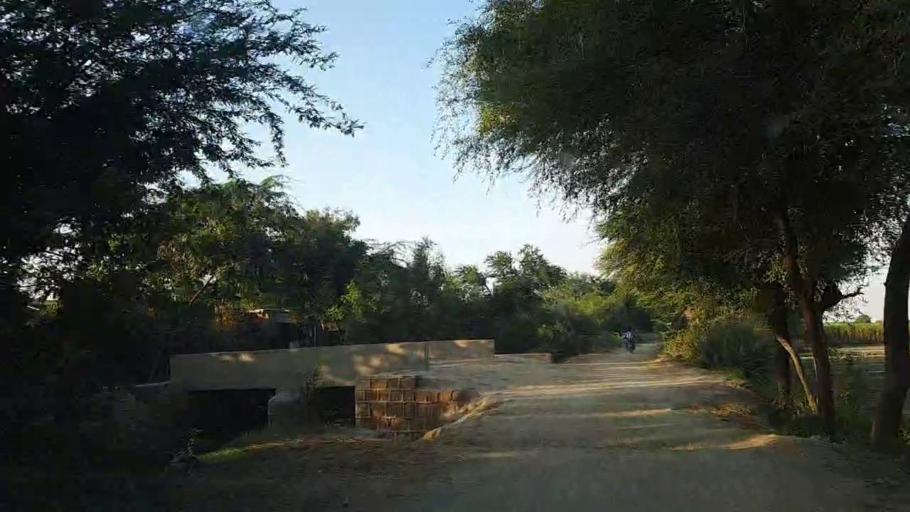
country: PK
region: Sindh
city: Mirpur Batoro
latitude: 24.7124
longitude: 68.2145
